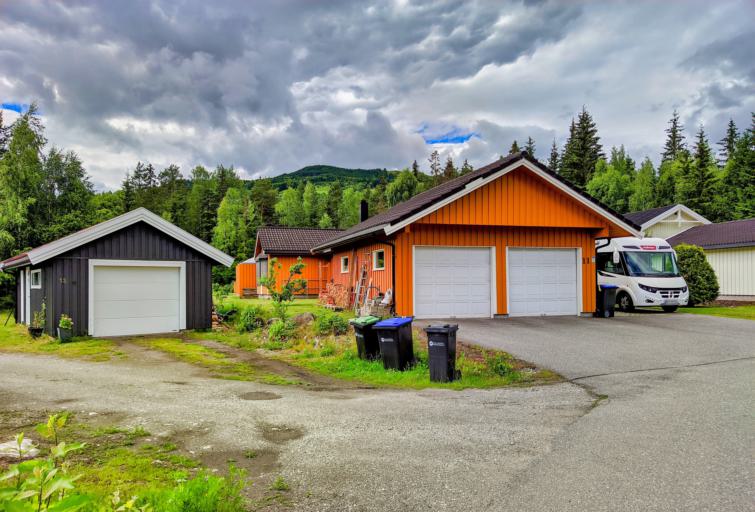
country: NO
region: Buskerud
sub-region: Gol
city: Gol
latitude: 60.7074
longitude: 8.9336
